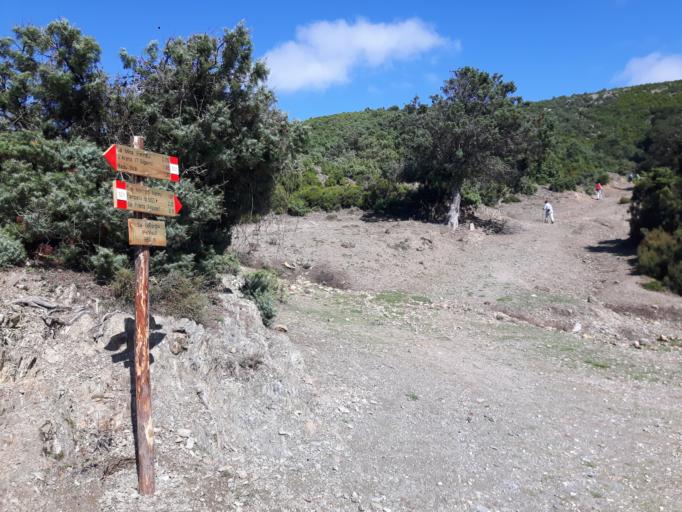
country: IT
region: Sardinia
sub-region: Provincia di Ogliastra
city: Urzulei
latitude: 40.0933
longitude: 9.4626
